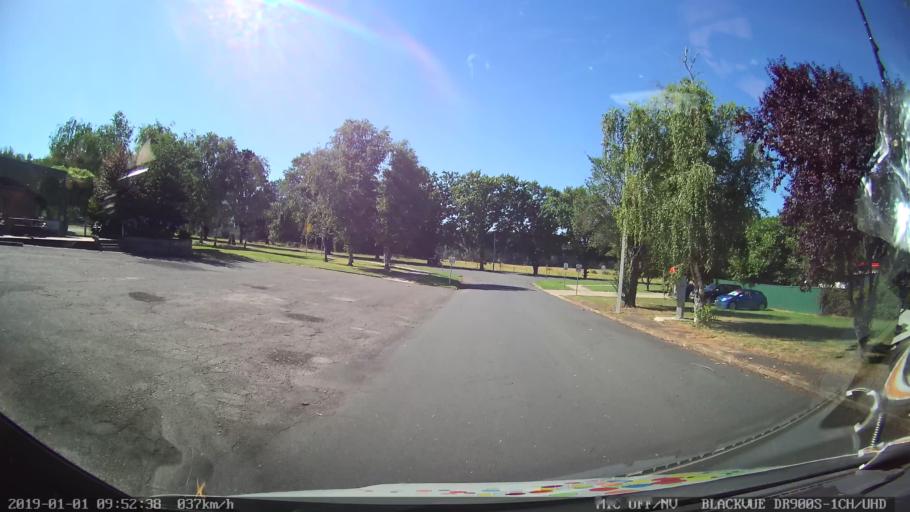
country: AU
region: New South Wales
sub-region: Snowy River
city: Jindabyne
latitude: -36.2189
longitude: 148.1247
